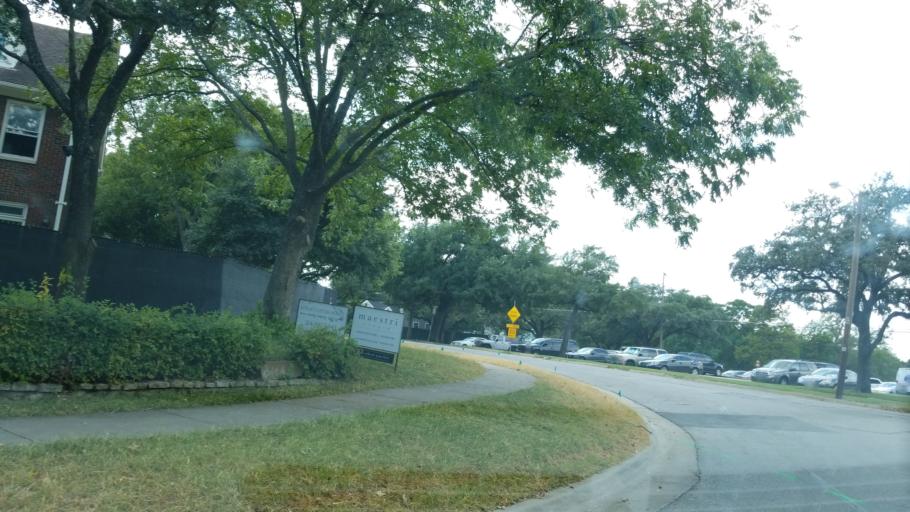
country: US
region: Texas
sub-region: Dallas County
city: Cockrell Hill
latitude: 32.7563
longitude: -96.8462
